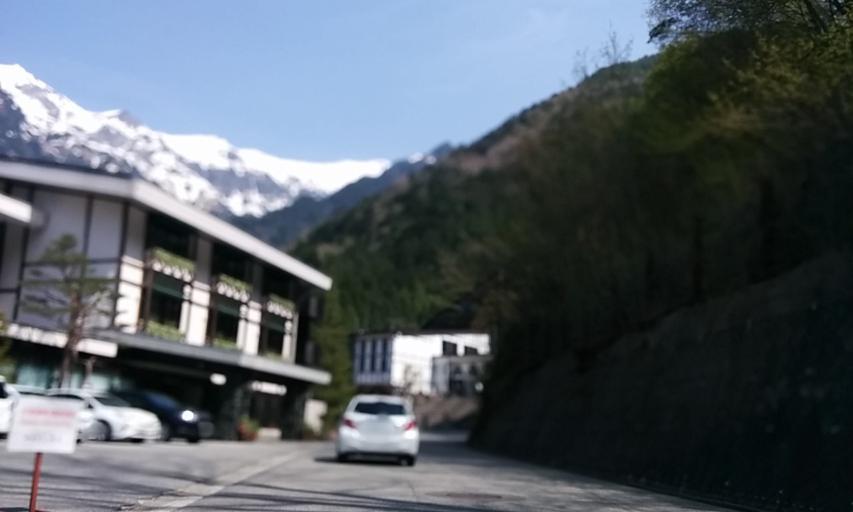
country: JP
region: Nagano
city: Hotaka
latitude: 36.2850
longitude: 137.5753
